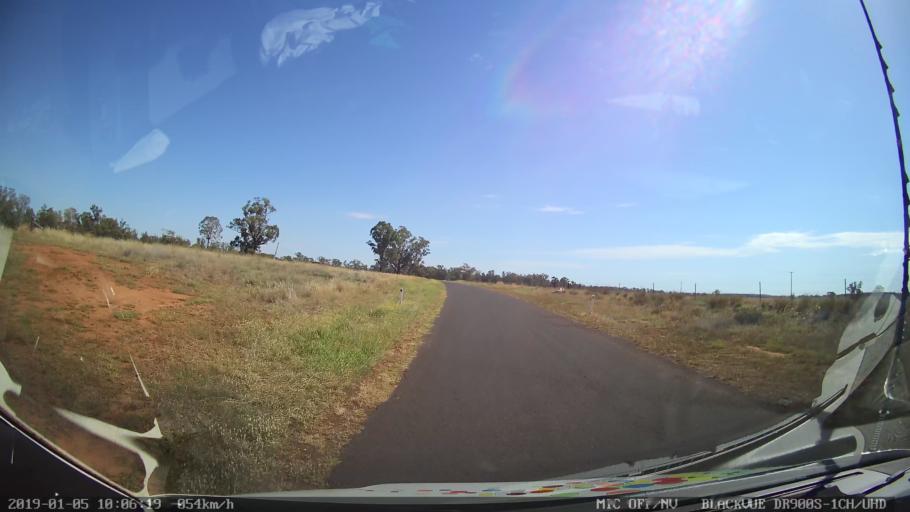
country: AU
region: New South Wales
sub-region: Gilgandra
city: Gilgandra
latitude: -31.6590
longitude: 148.8695
